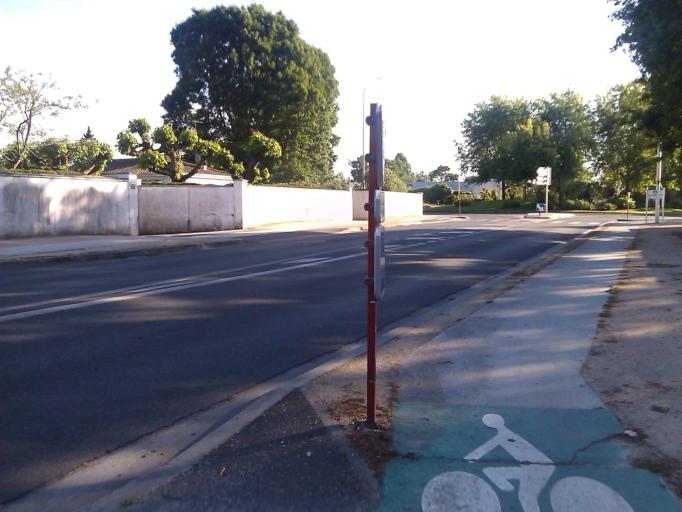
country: FR
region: Aquitaine
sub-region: Departement de la Gironde
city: Cestas
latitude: 44.7866
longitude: -0.6802
